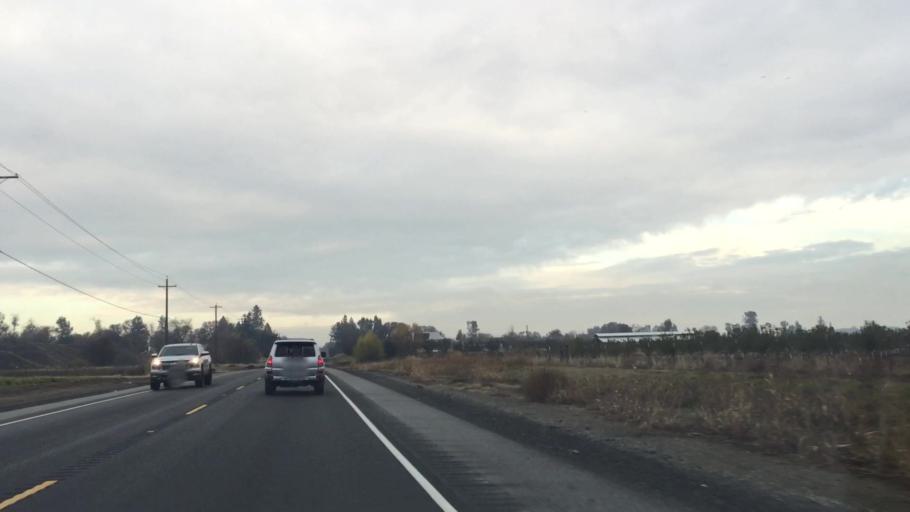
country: US
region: California
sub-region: Butte County
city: Palermo
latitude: 39.4214
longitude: -121.6050
